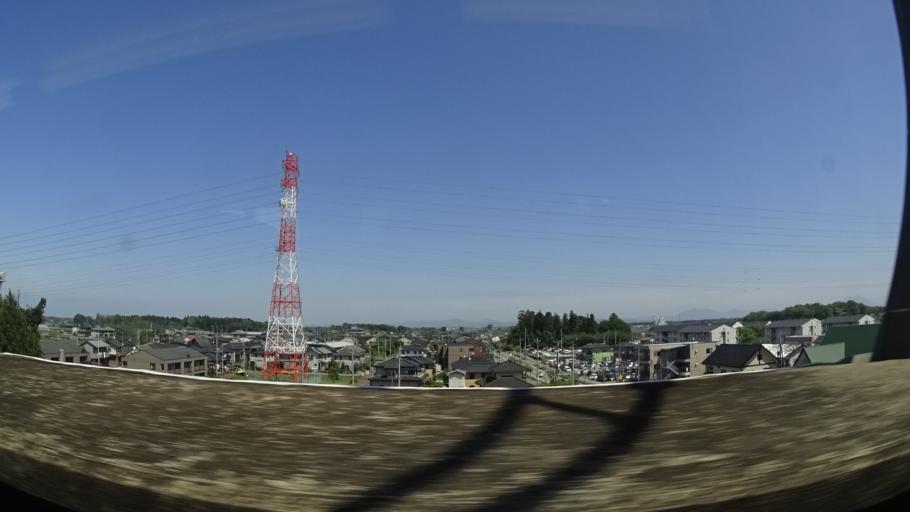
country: JP
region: Tochigi
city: Kaminokawa
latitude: 36.4375
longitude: 139.8670
